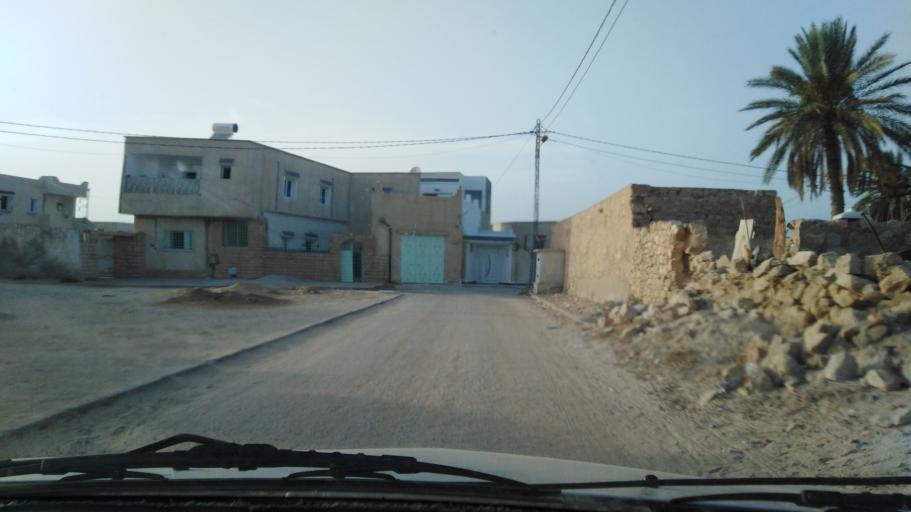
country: TN
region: Qabis
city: Gabes
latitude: 33.9554
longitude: 9.9961
